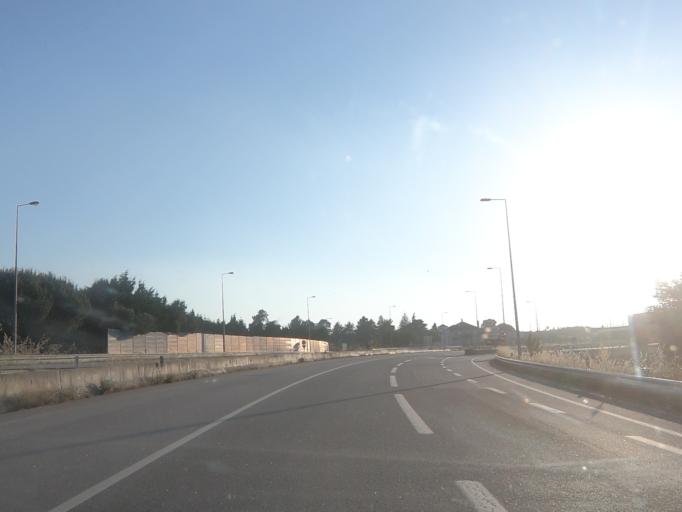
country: PT
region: Guarda
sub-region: Celorico da Beira
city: Celorico da Beira
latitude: 40.6241
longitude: -7.3983
